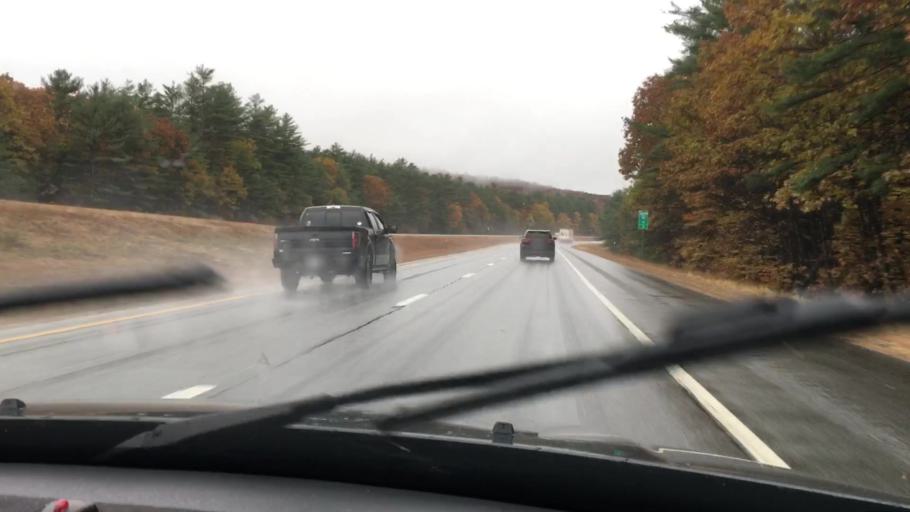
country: US
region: New Hampshire
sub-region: Grafton County
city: Ashland
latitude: 43.6490
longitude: -71.6478
